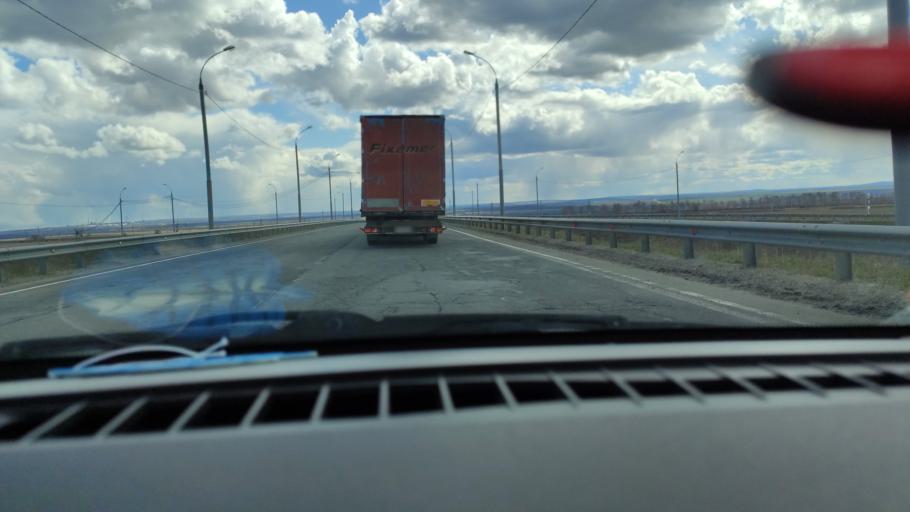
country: RU
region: Samara
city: Varlamovo
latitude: 53.1918
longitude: 48.2922
